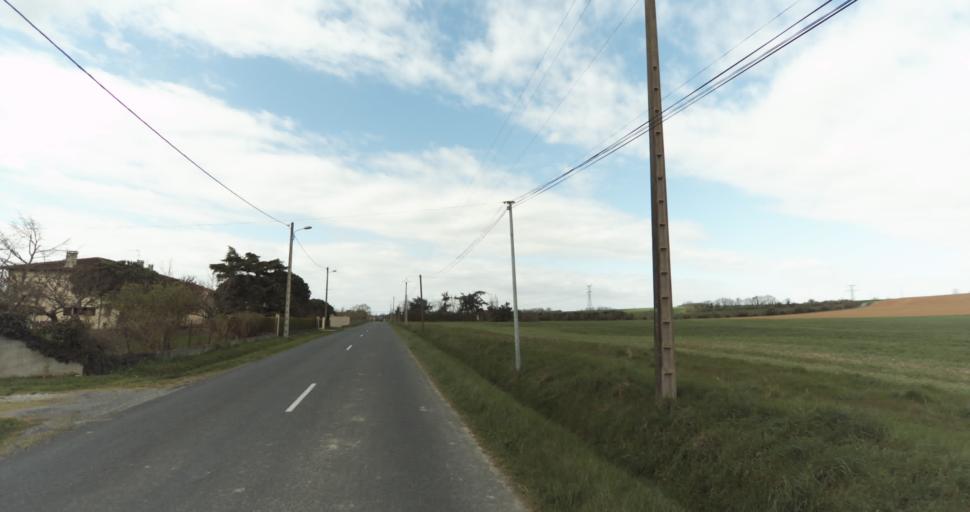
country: FR
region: Midi-Pyrenees
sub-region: Departement de la Haute-Garonne
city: Auterive
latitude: 43.3791
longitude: 1.4622
